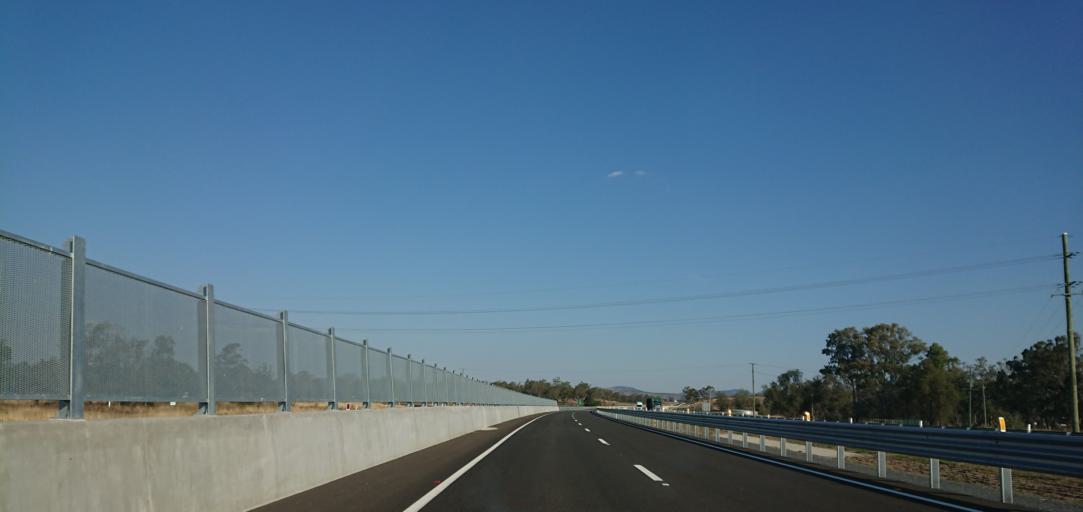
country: AU
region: Queensland
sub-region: Toowoomba
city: East Toowoomba
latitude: -27.5303
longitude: 152.0732
